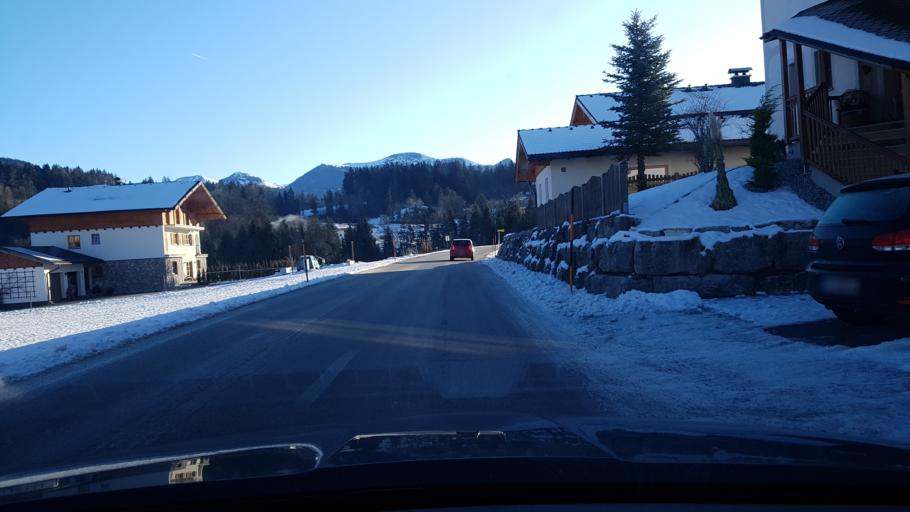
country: AT
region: Salzburg
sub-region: Politischer Bezirk Hallein
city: Kuchl
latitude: 47.6600
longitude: 13.1748
